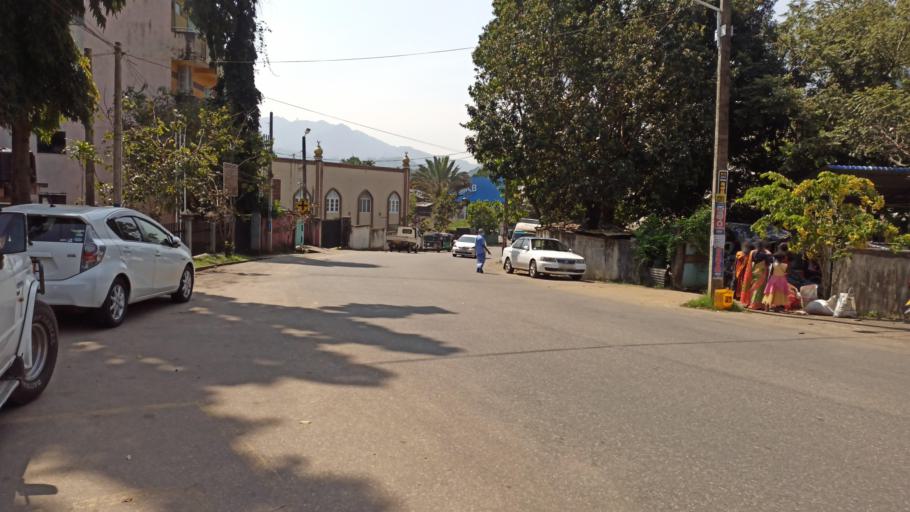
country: LK
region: Uva
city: Badulla
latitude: 6.9898
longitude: 81.0595
